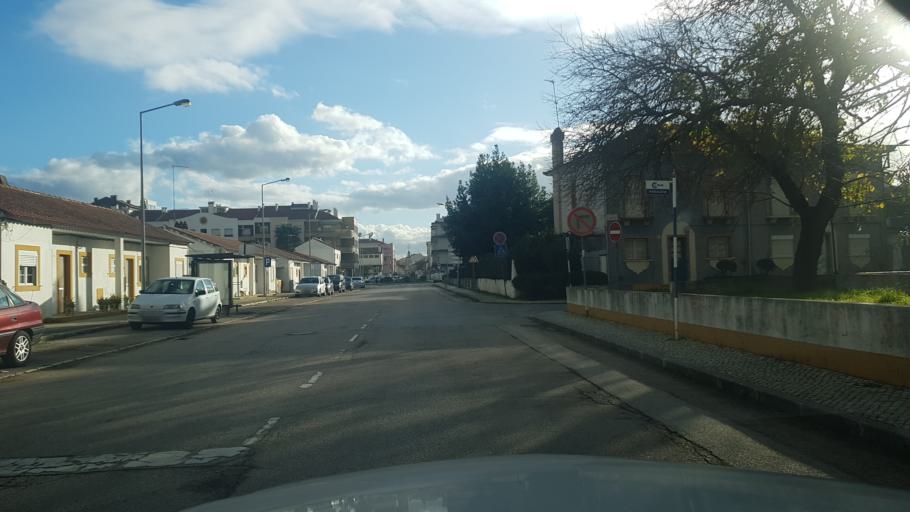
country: PT
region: Santarem
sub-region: Entroncamento
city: Entroncamento
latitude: 39.4697
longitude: -8.4731
